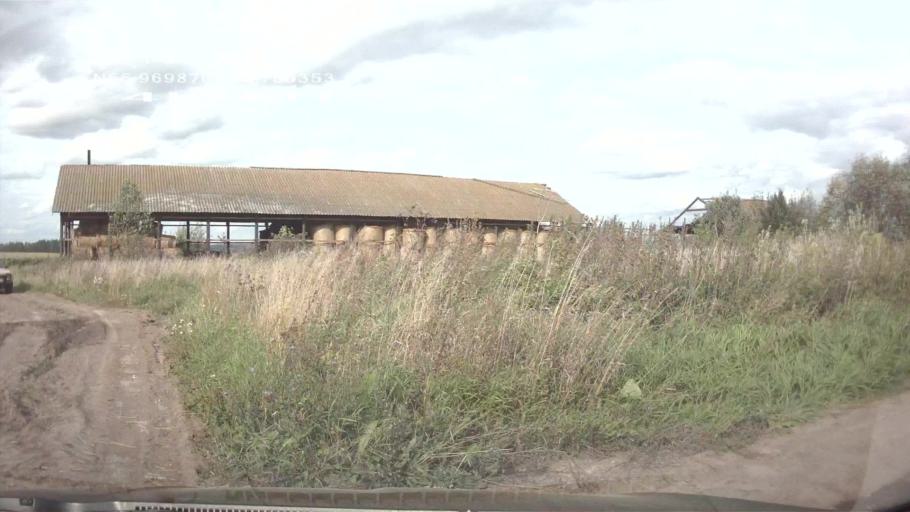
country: RU
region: Mariy-El
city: Kuzhener
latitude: 56.9699
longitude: 48.7863
